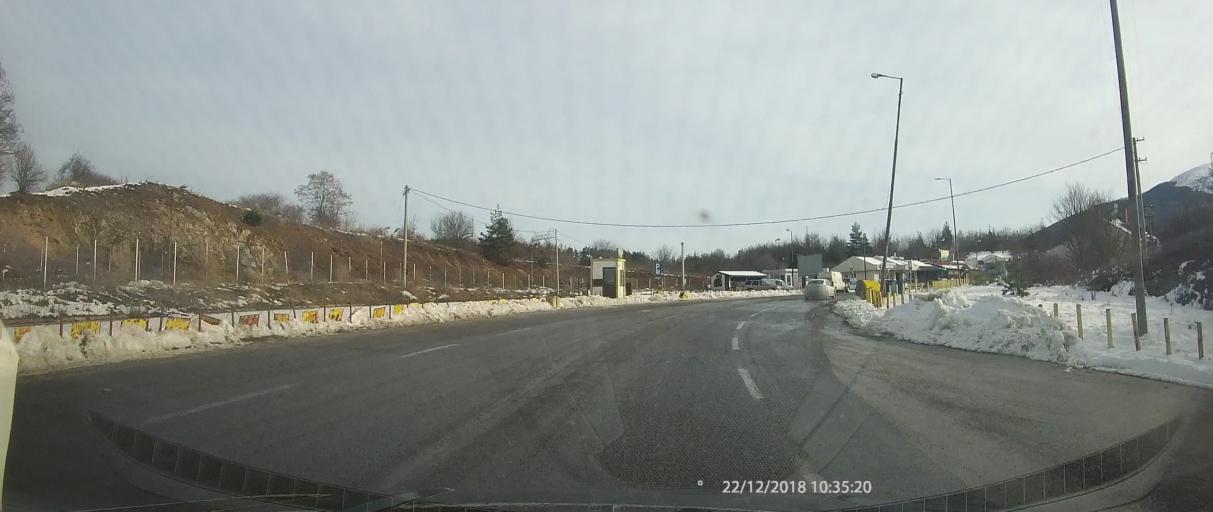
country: MK
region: Kriva Palanka
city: Kriva Palanka
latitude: 42.2220
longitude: 22.4547
